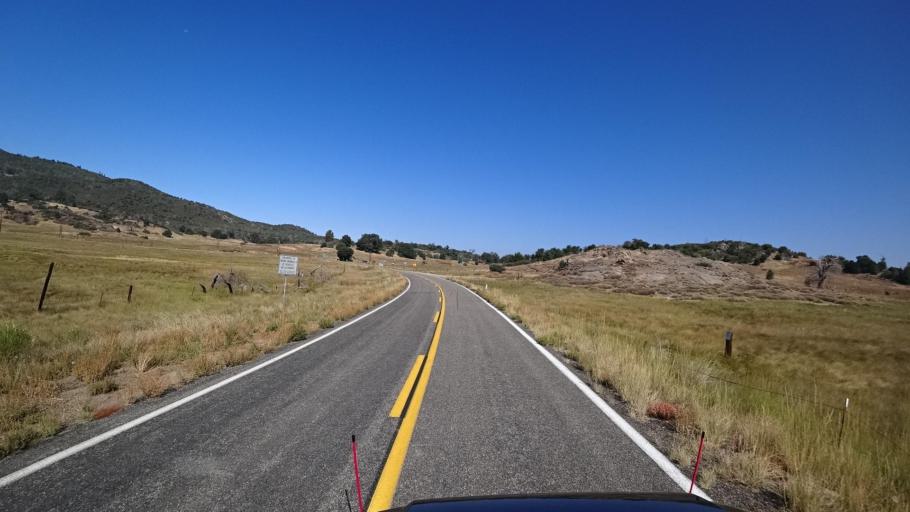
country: US
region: California
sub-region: San Diego County
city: Julian
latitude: 33.0095
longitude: -116.5589
